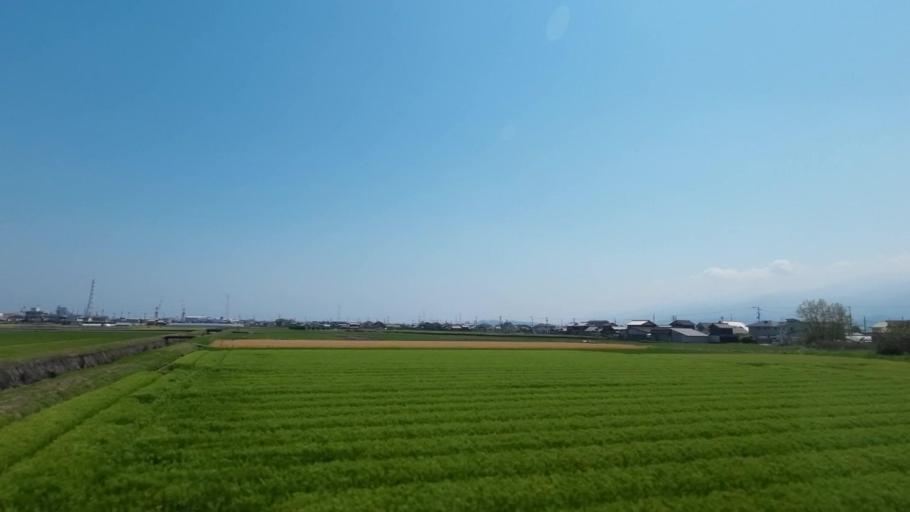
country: JP
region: Ehime
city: Saijo
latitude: 33.9147
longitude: 133.0986
